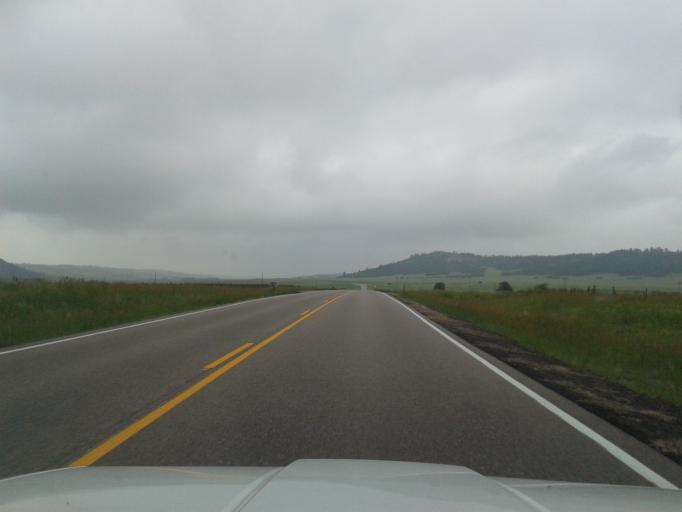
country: US
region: Colorado
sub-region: El Paso County
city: Woodmoor
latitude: 39.1481
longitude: -104.7591
